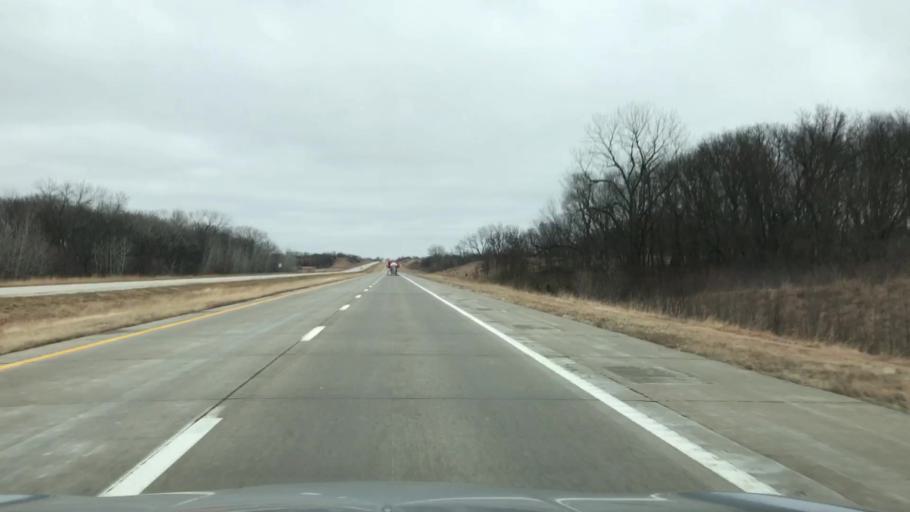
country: US
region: Missouri
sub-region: Caldwell County
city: Hamilton
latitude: 39.7342
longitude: -93.9697
